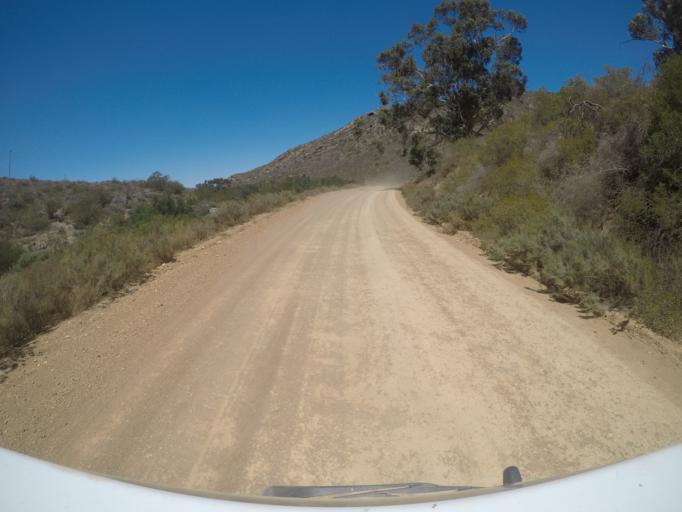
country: ZA
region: Western Cape
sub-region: Overberg District Municipality
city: Caledon
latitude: -34.1188
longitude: 19.2356
